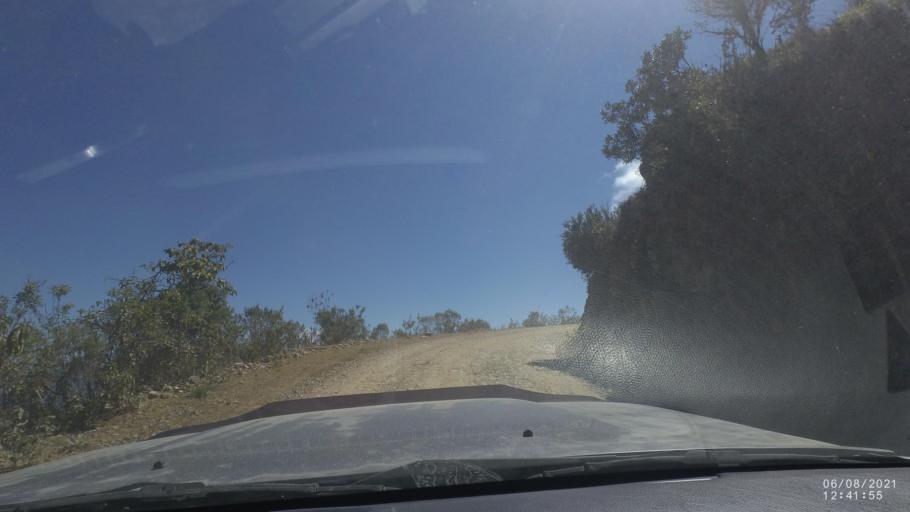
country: BO
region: Cochabamba
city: Colchani
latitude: -16.7802
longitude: -66.6660
